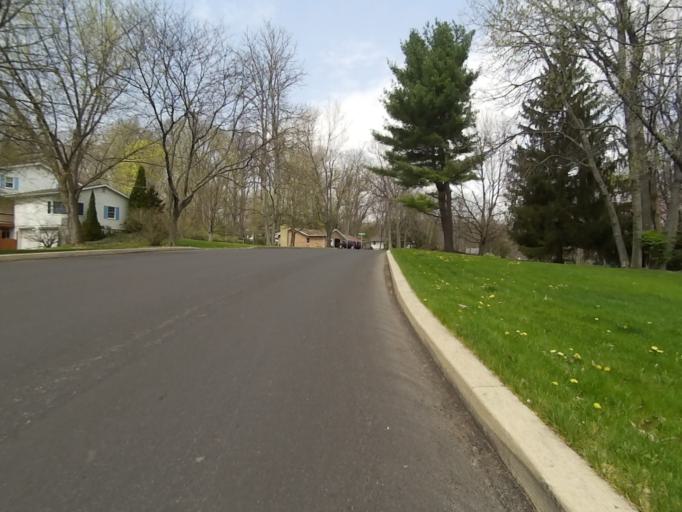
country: US
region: Pennsylvania
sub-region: Centre County
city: Park Forest Village
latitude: 40.7957
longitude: -77.9018
